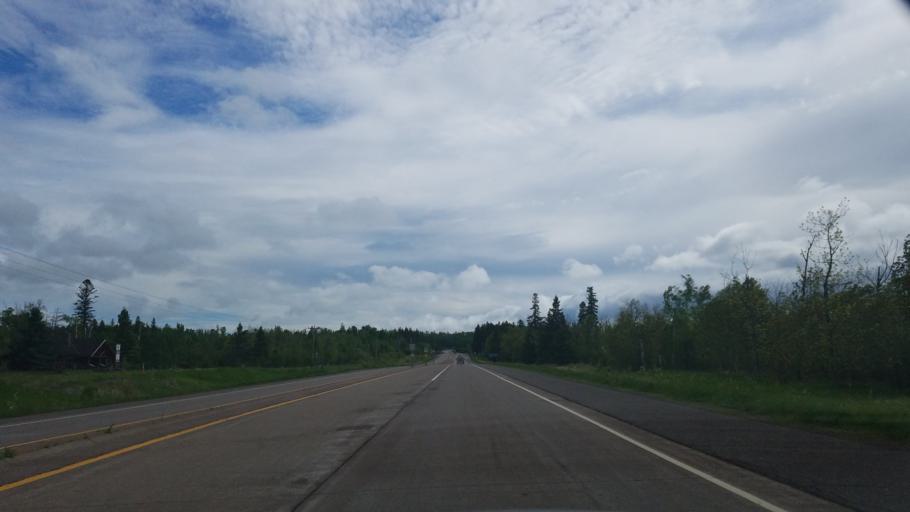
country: US
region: Minnesota
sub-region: Lake County
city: Two Harbors
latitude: 47.1362
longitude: -91.4784
